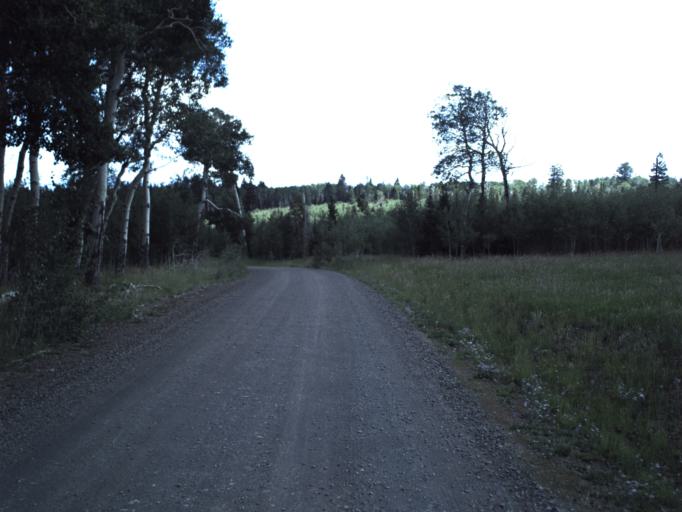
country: US
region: Utah
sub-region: Piute County
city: Junction
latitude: 38.2504
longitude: -112.3377
